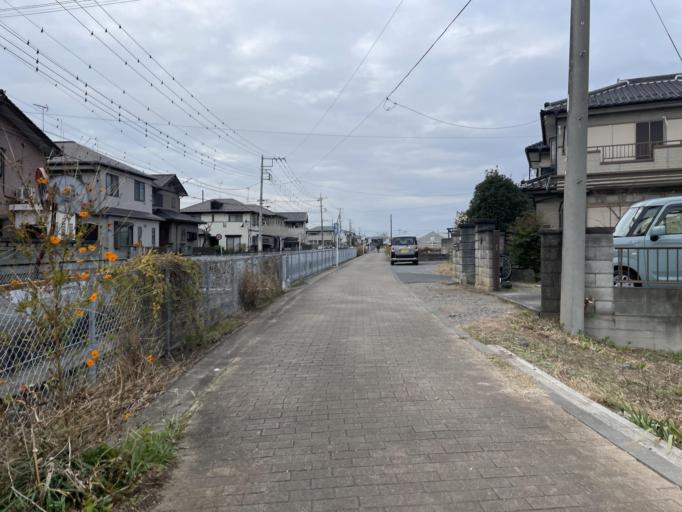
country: JP
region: Saitama
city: Shiraoka
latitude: 36.0212
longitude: 139.6630
